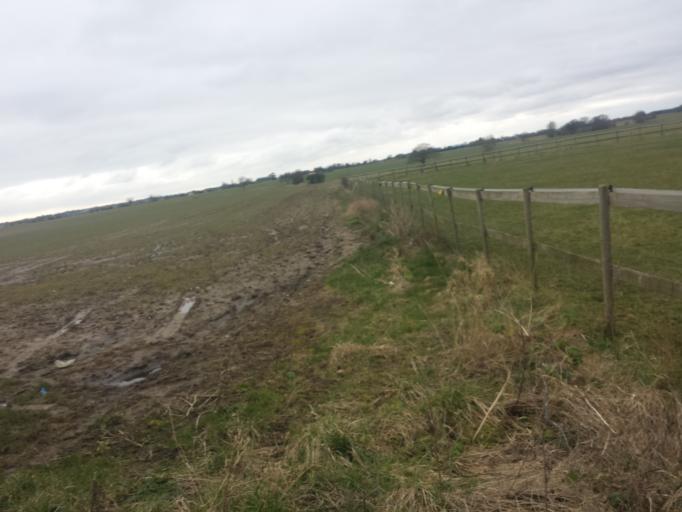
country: GB
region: England
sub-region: Essex
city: Little Clacton
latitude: 51.8958
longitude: 1.1842
